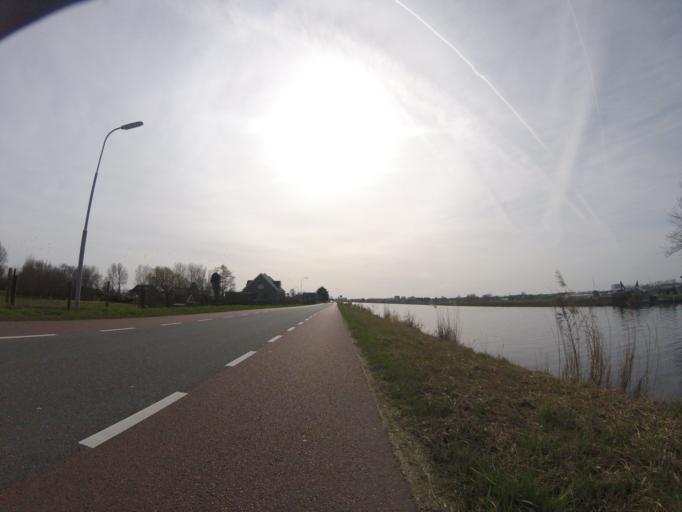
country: NL
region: North Holland
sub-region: Gemeente Bloemendaal
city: Bennebroek
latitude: 52.3042
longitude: 4.6037
